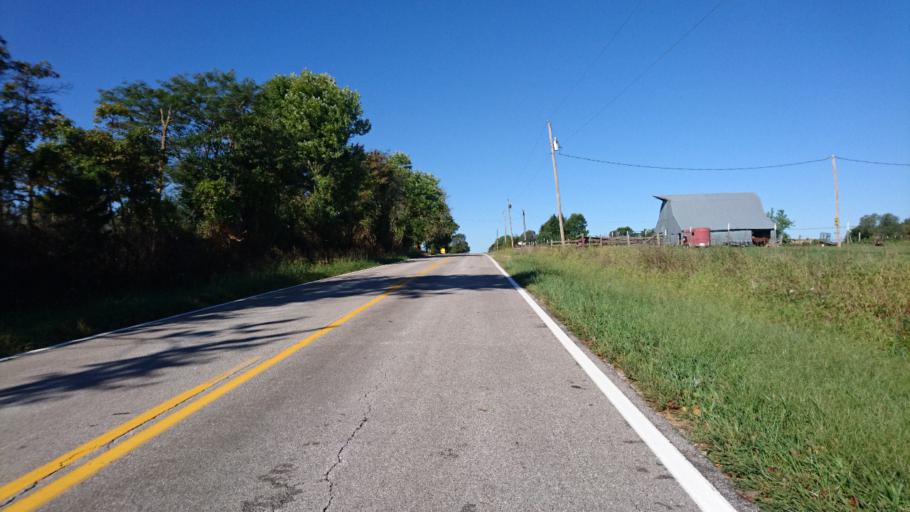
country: US
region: Missouri
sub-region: Greene County
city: Ash Grove
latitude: 37.1938
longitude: -93.6511
